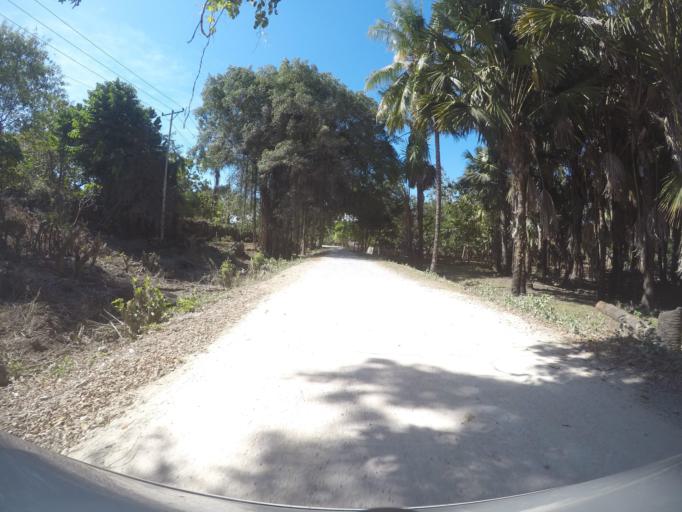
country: TL
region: Viqueque
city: Viqueque
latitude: -8.8986
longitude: 126.5069
